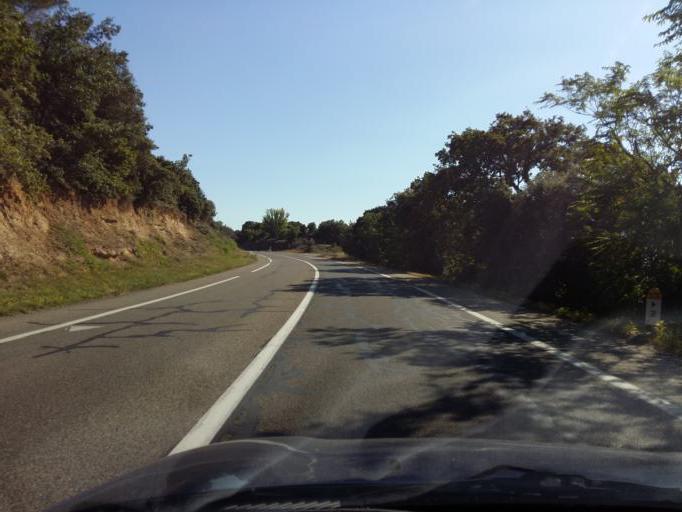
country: FR
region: Provence-Alpes-Cote d'Azur
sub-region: Departement du Vaucluse
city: Visan
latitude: 44.3492
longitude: 4.9568
